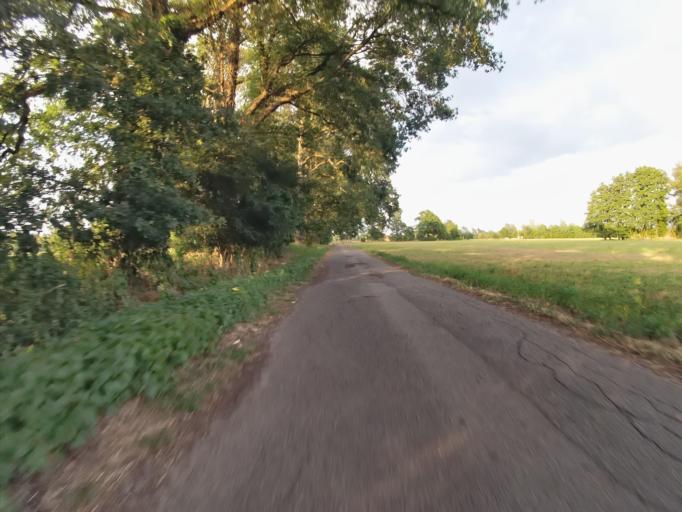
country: DE
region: North Rhine-Westphalia
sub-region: Regierungsbezirk Munster
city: Westerkappeln
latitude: 52.3541
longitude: 7.8988
